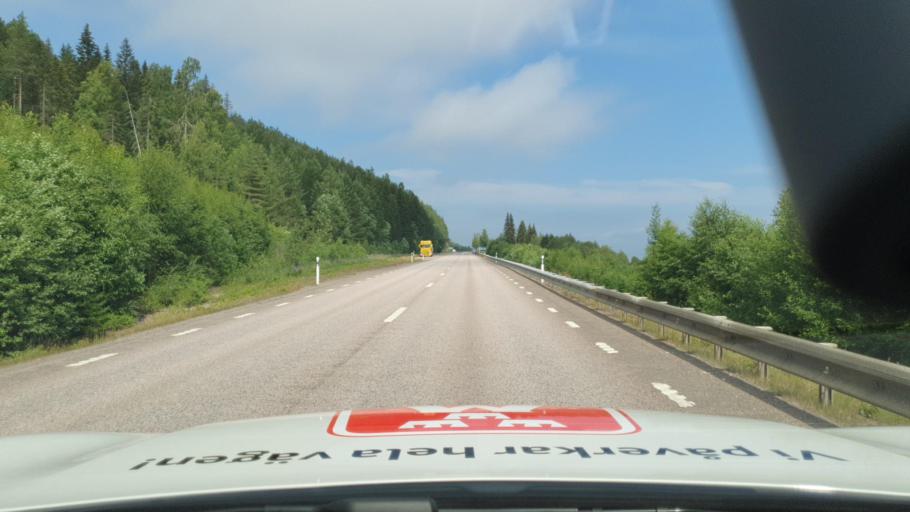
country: SE
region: Vaermland
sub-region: Sunne Kommun
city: Sunne
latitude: 59.9798
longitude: 13.1027
